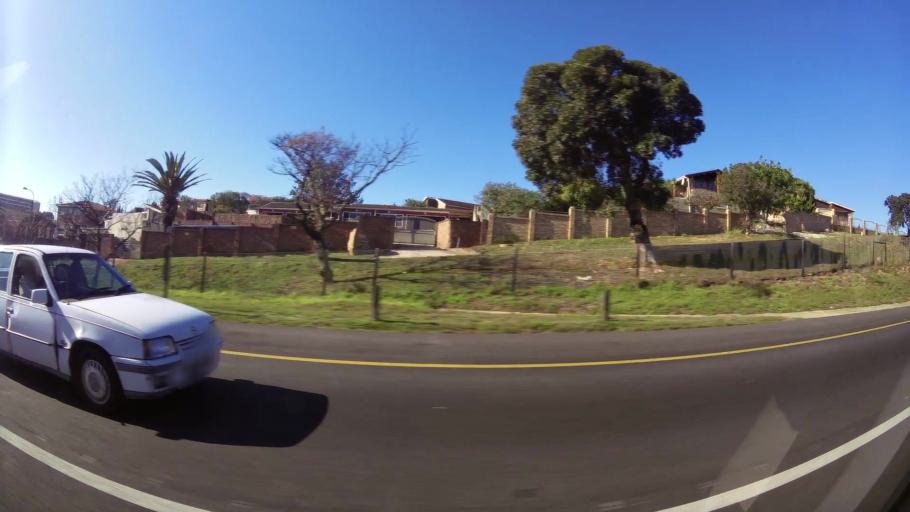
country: ZA
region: Eastern Cape
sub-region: Nelson Mandela Bay Metropolitan Municipality
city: Port Elizabeth
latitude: -33.9363
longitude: 25.5558
